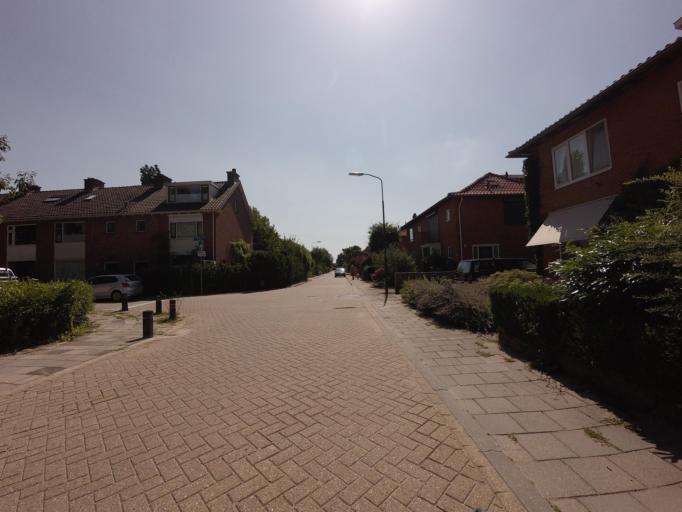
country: NL
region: Utrecht
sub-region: Gemeente Bunnik
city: Bunnik
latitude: 52.0662
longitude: 5.2073
